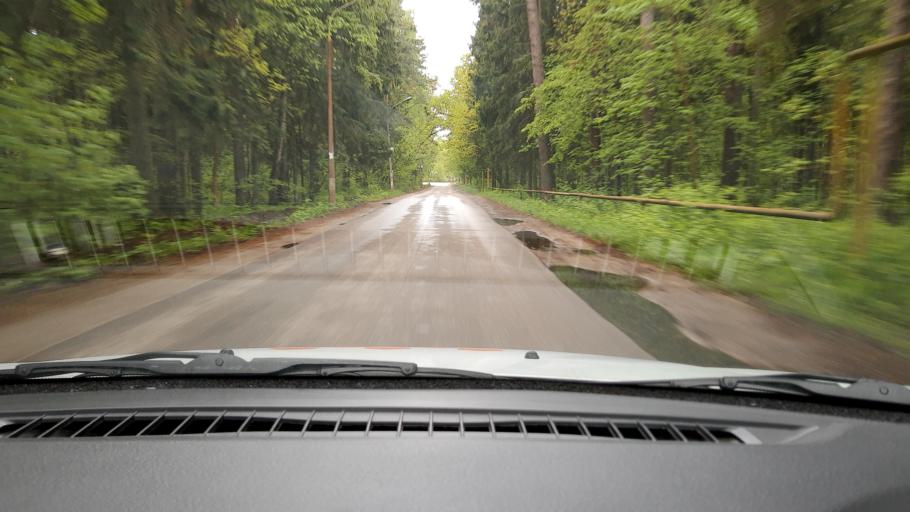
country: RU
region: Nizjnij Novgorod
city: Afonino
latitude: 56.1779
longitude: 44.0777
